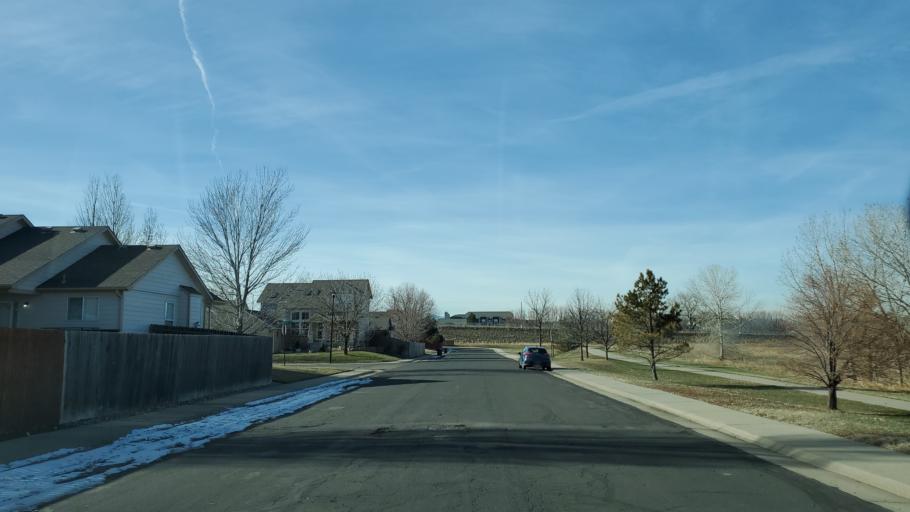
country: US
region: Colorado
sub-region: Adams County
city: Northglenn
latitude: 39.9169
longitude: -104.9554
